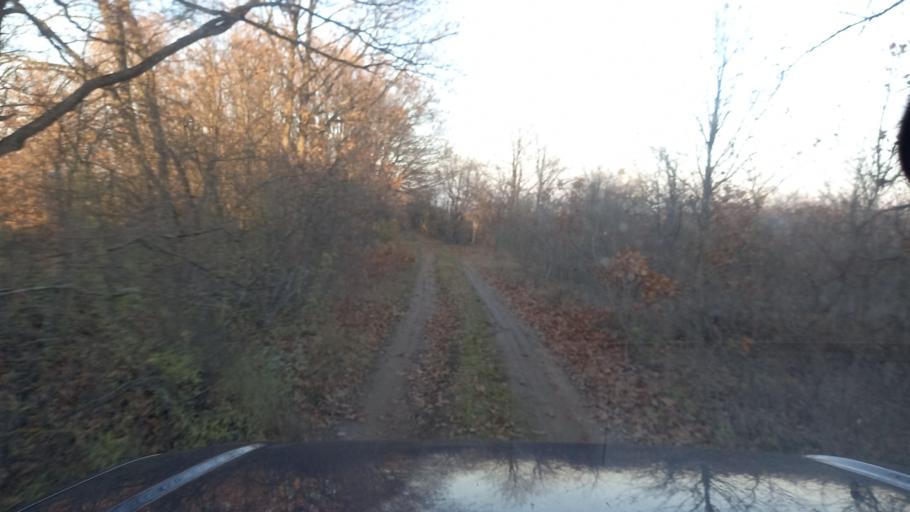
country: RU
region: Krasnodarskiy
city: Azovskaya
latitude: 44.8134
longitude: 38.6050
